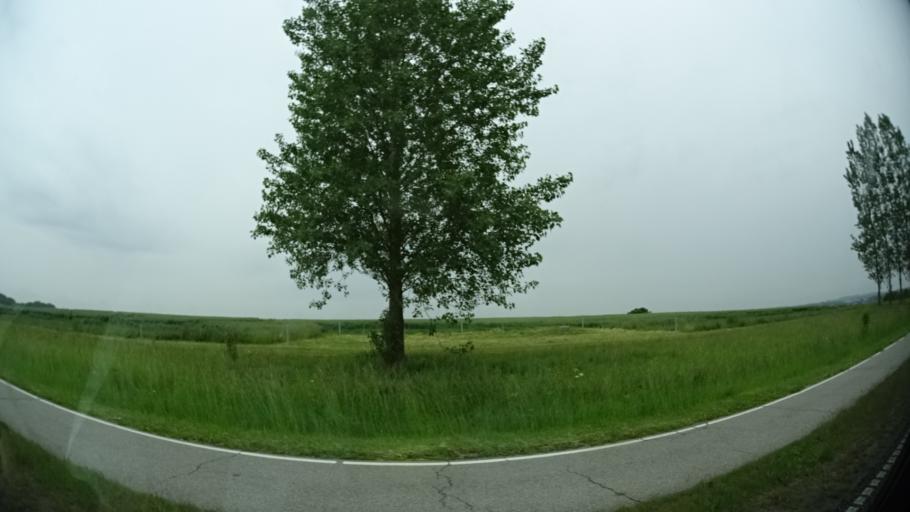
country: DK
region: Central Jutland
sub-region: Arhus Kommune
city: Hjortshoj
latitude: 56.2196
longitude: 10.2847
